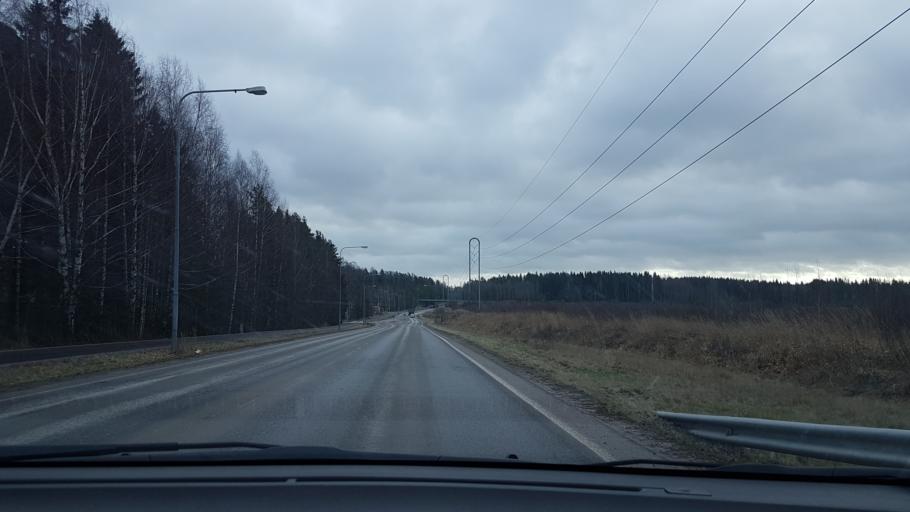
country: FI
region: Uusimaa
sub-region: Helsinki
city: Tuusula
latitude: 60.3809
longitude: 25.0452
